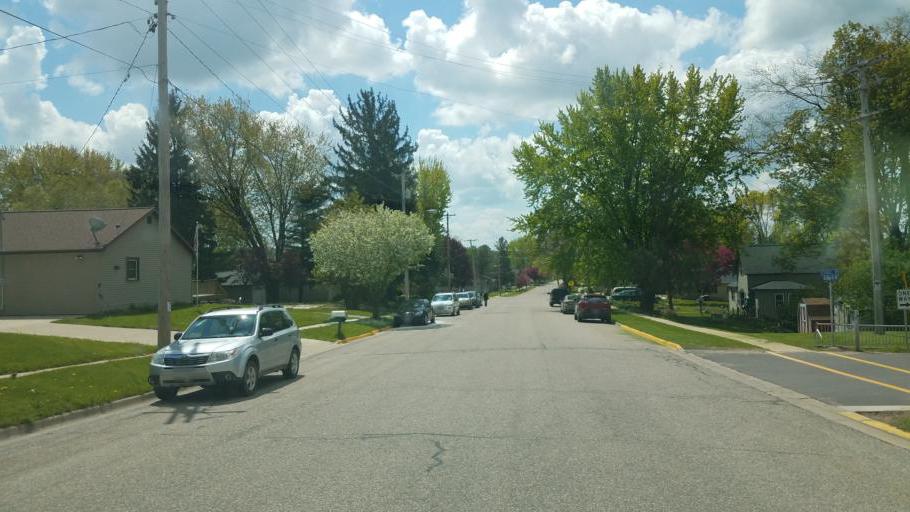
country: US
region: Wisconsin
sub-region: Vernon County
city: Hillsboro
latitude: 43.6579
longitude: -90.3488
